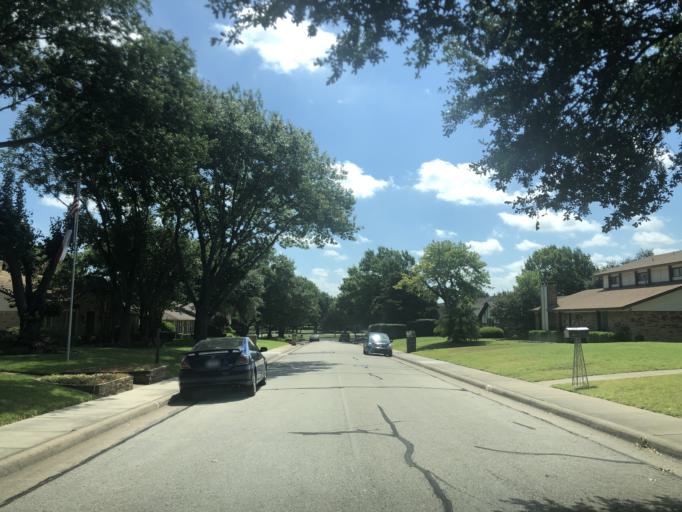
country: US
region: Texas
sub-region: Dallas County
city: Duncanville
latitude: 32.6488
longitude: -96.9316
